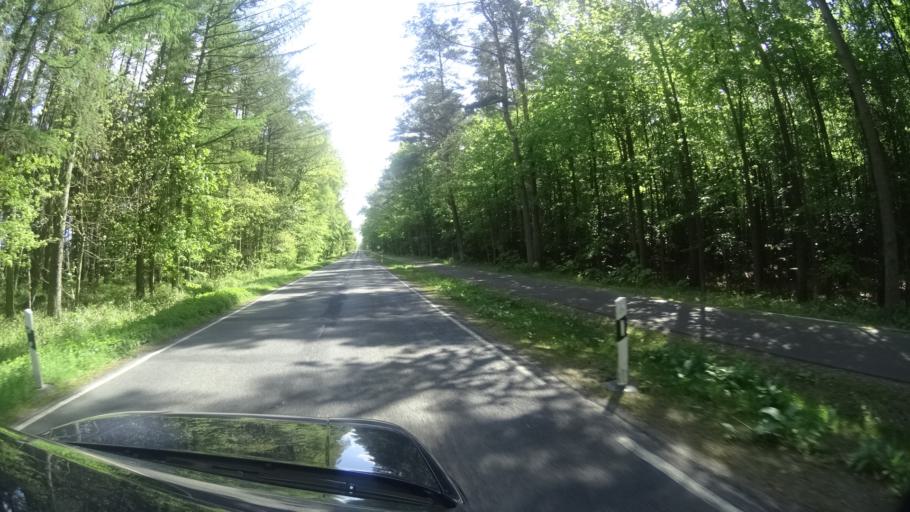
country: DE
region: Mecklenburg-Vorpommern
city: Barth
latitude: 54.3636
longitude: 12.6519
